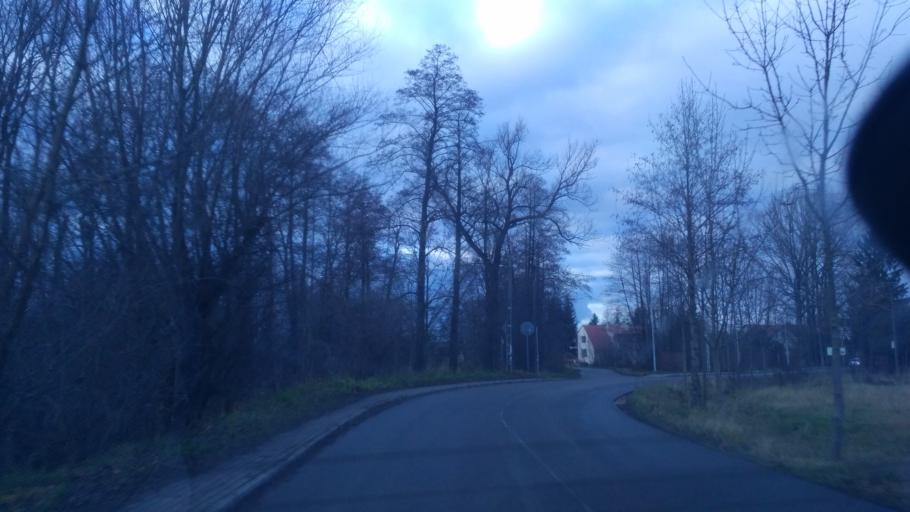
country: PL
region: Subcarpathian Voivodeship
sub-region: Powiat rzeszowski
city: Krasne
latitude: 50.0715
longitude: 22.1134
